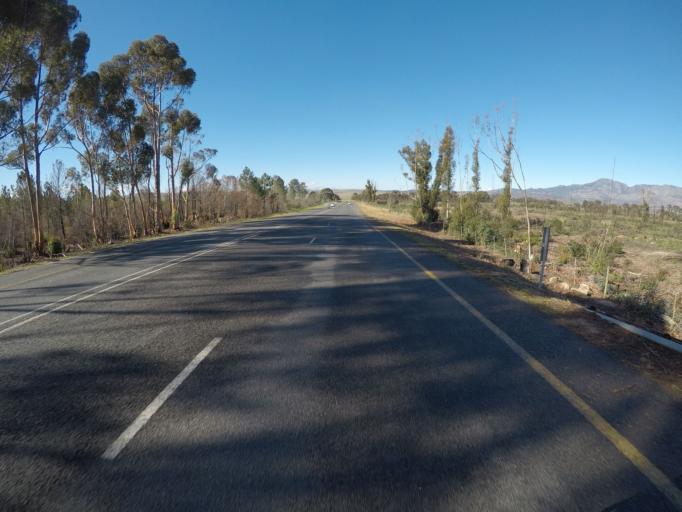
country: ZA
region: Western Cape
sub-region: Overberg District Municipality
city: Hermanus
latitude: -34.2351
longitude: 19.1957
